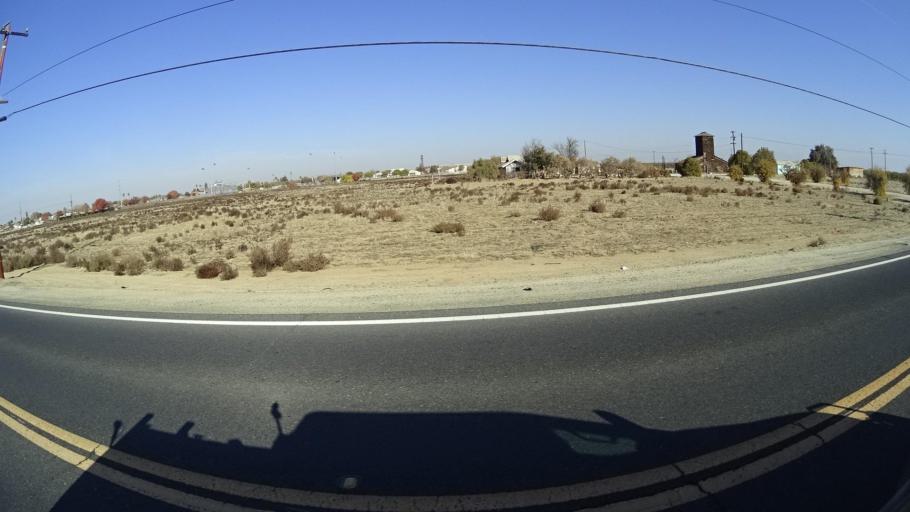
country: US
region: California
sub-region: Kern County
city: Delano
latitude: 35.7617
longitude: -119.2205
